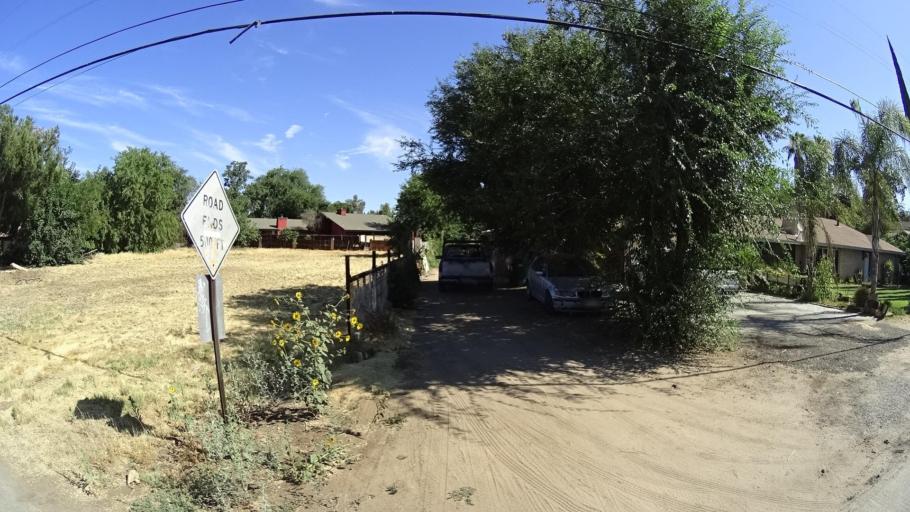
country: US
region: California
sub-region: Fresno County
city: Sunnyside
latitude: 36.7377
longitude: -119.7028
